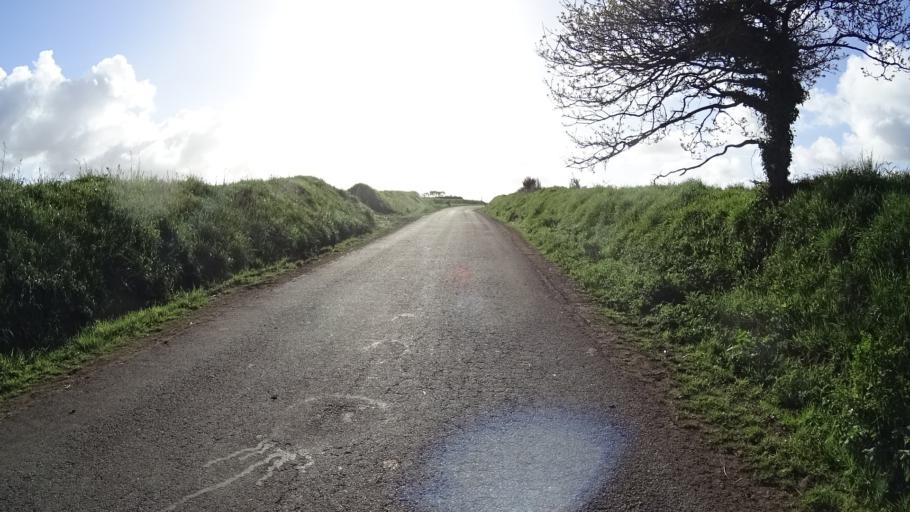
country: FR
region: Brittany
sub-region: Departement du Finistere
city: Ploumoguer
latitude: 48.4245
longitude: -4.7042
